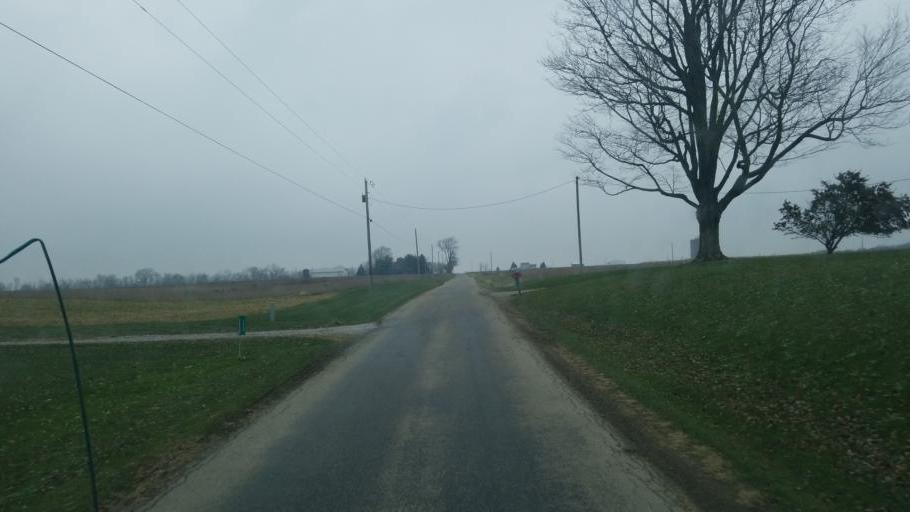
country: US
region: Ohio
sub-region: Huron County
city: New London
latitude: 41.0404
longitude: -82.3260
